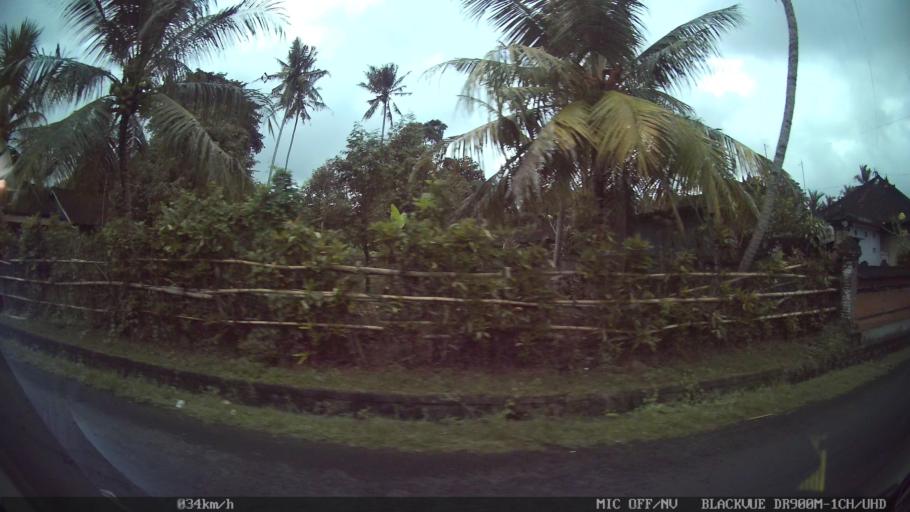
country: ID
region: Bali
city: Banjar Parekan
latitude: -8.5609
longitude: 115.2070
